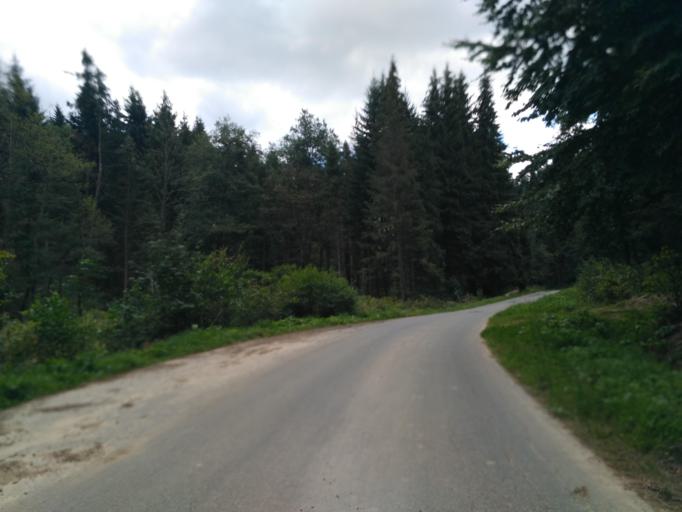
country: PL
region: Subcarpathian Voivodeship
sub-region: Powiat rzeszowski
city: Dynow
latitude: 49.7518
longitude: 22.2943
